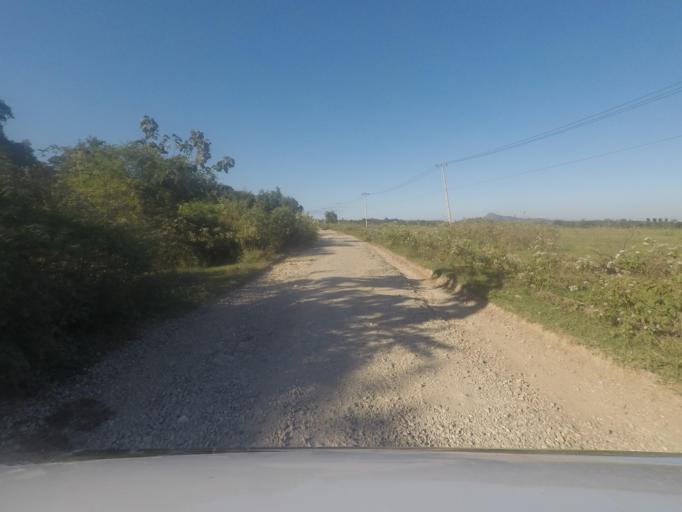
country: TL
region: Lautem
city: Lospalos
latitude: -8.4067
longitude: 127.1731
